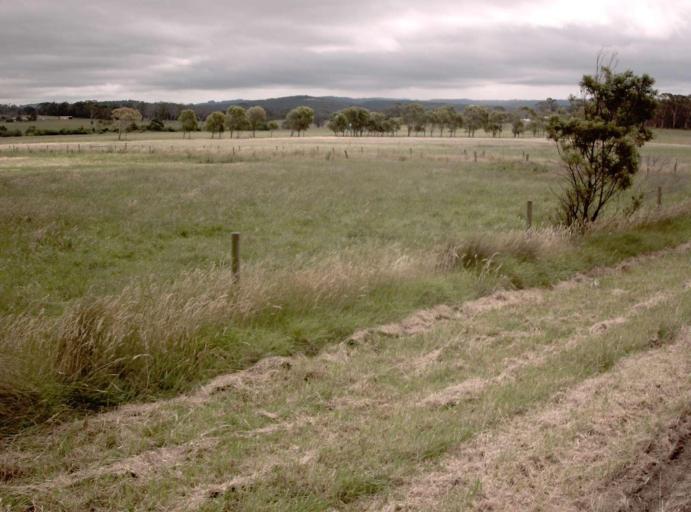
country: AU
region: Victoria
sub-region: Latrobe
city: Traralgon
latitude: -38.5480
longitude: 146.6551
